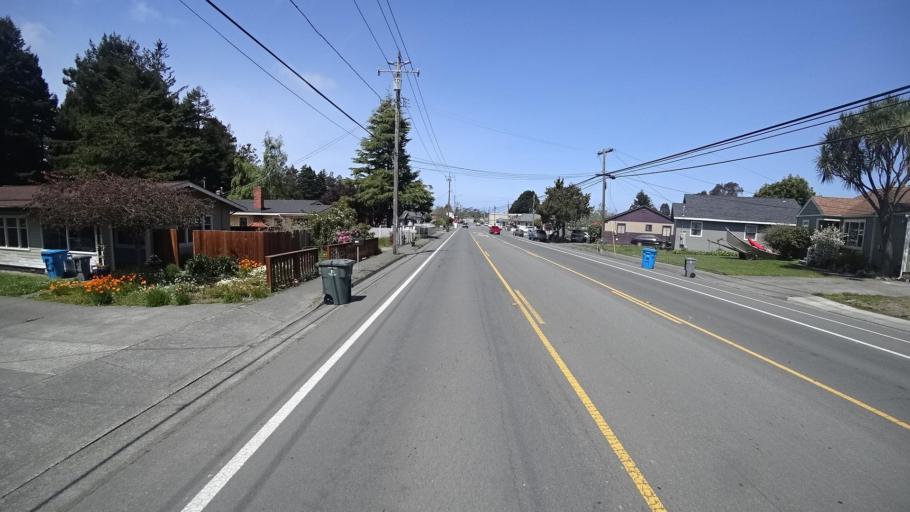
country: US
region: California
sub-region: Humboldt County
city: Myrtletown
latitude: 40.7925
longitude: -124.1349
